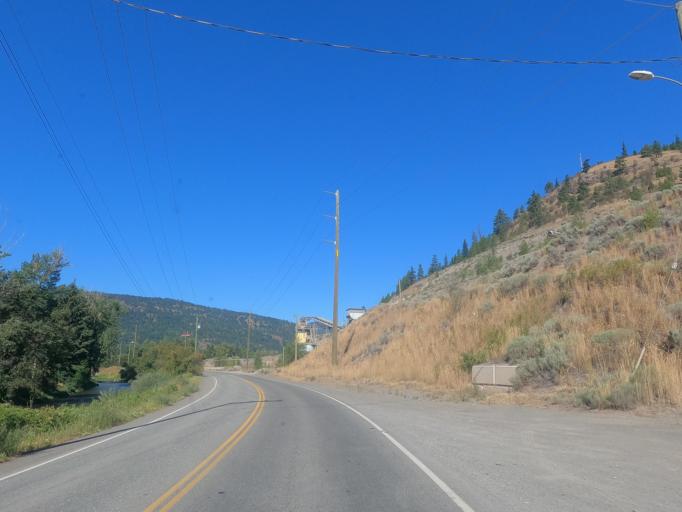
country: CA
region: British Columbia
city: Merritt
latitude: 50.1158
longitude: -120.8009
